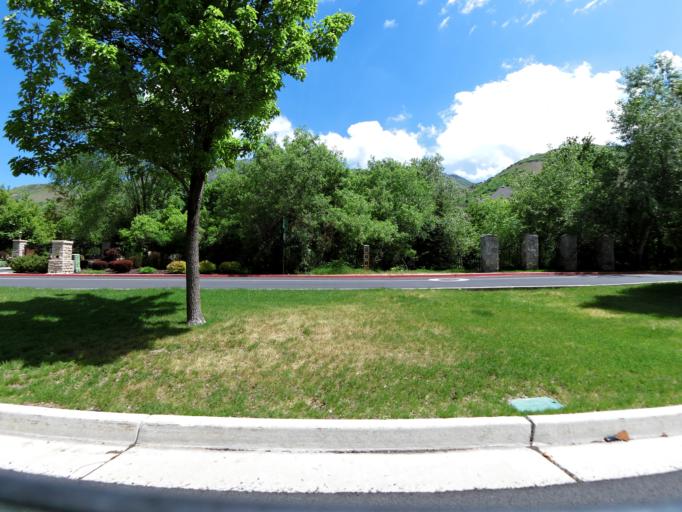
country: US
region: Utah
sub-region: Weber County
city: Uintah
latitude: 41.1706
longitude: -111.9290
